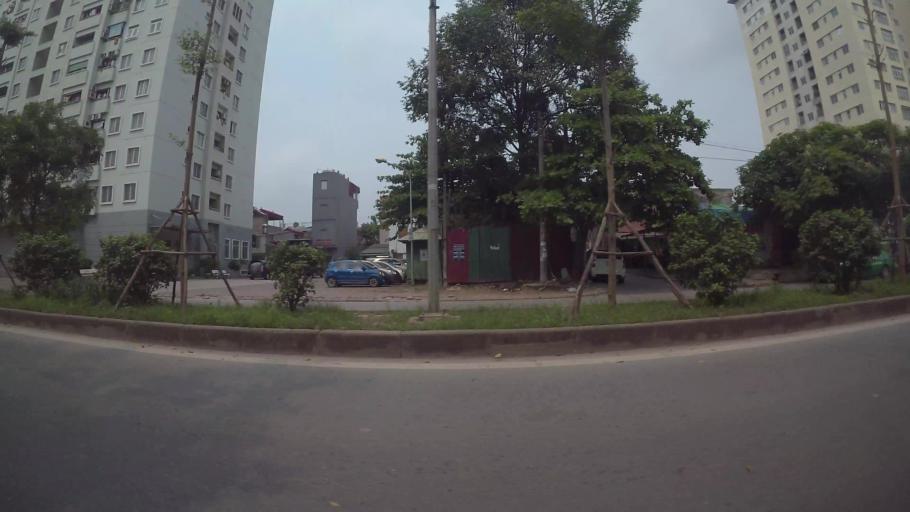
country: VN
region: Ha Noi
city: Trau Quy
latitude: 21.0683
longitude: 105.9039
